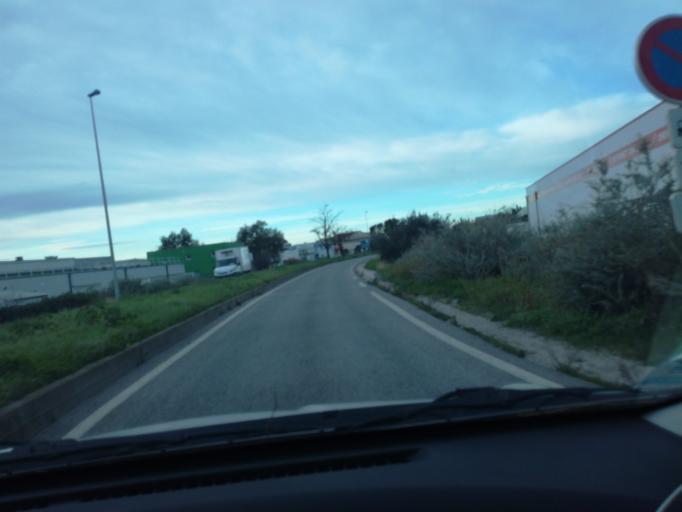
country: FR
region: Provence-Alpes-Cote d'Azur
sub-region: Departement du Var
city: La Farlede
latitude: 43.1561
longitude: 6.0491
